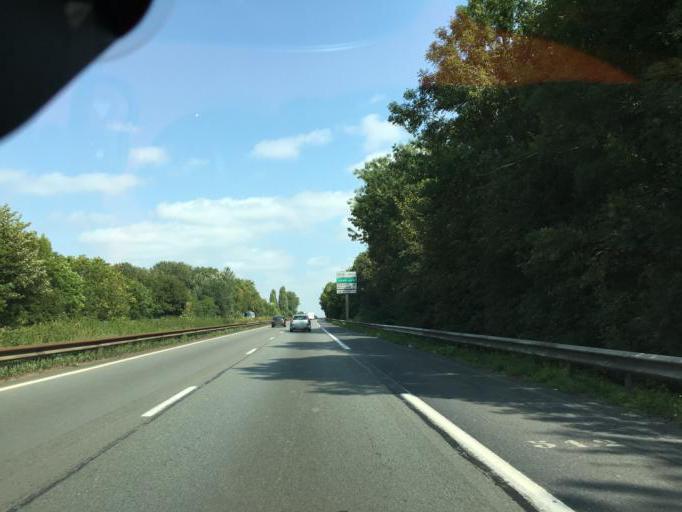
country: FR
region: Nord-Pas-de-Calais
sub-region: Departement du Nord
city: Douchy-les-Mines
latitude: 50.3101
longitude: 3.3904
